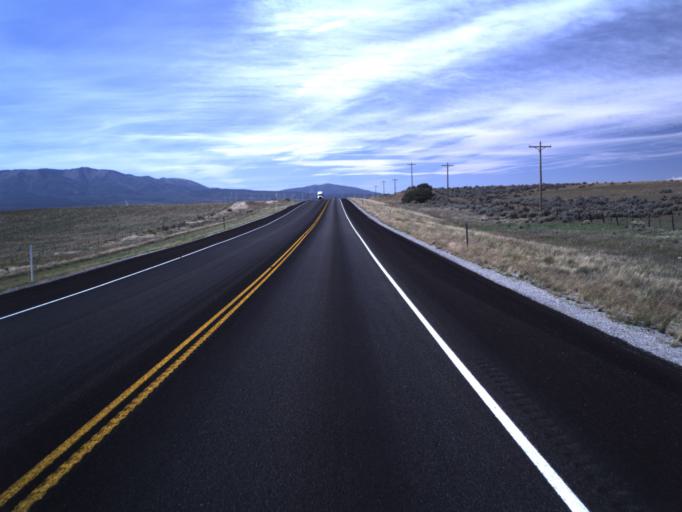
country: US
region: Utah
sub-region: San Juan County
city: Monticello
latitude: 37.8612
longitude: -109.2127
